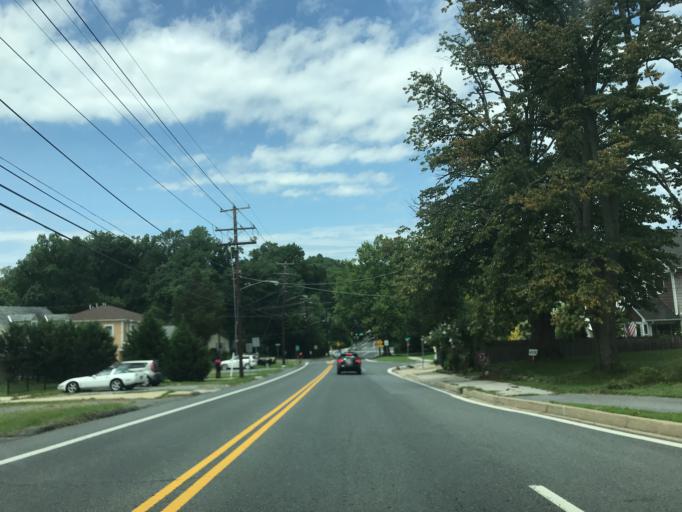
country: US
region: Maryland
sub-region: Montgomery County
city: Kensington
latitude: 39.0299
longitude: -77.0841
